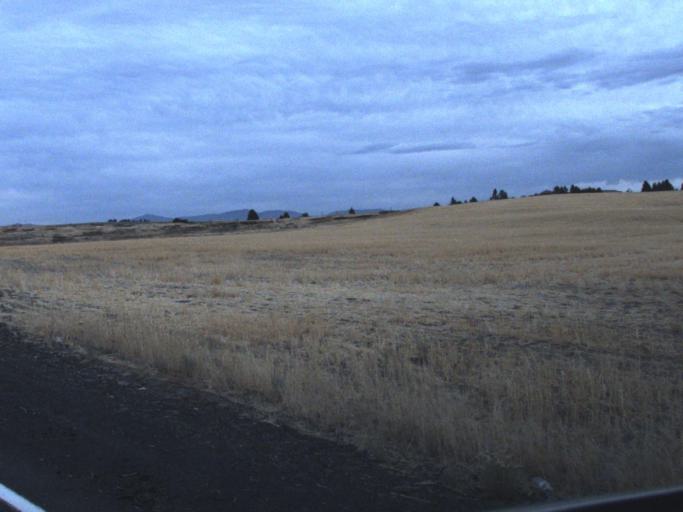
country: US
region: Washington
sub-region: Okanogan County
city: Coulee Dam
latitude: 47.7506
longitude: -118.7217
